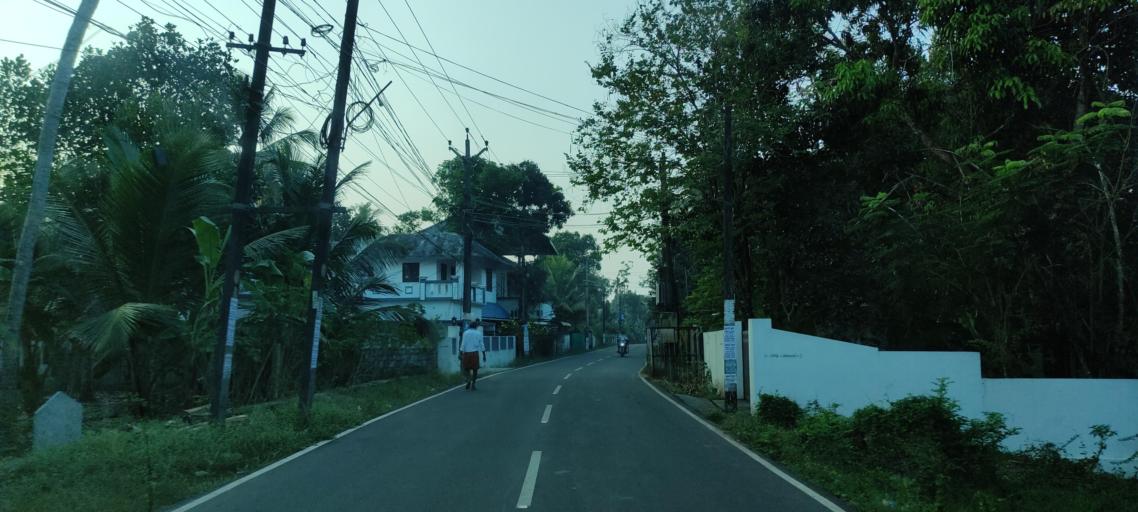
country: IN
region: Kerala
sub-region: Alappuzha
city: Alleppey
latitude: 9.4414
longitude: 76.3468
